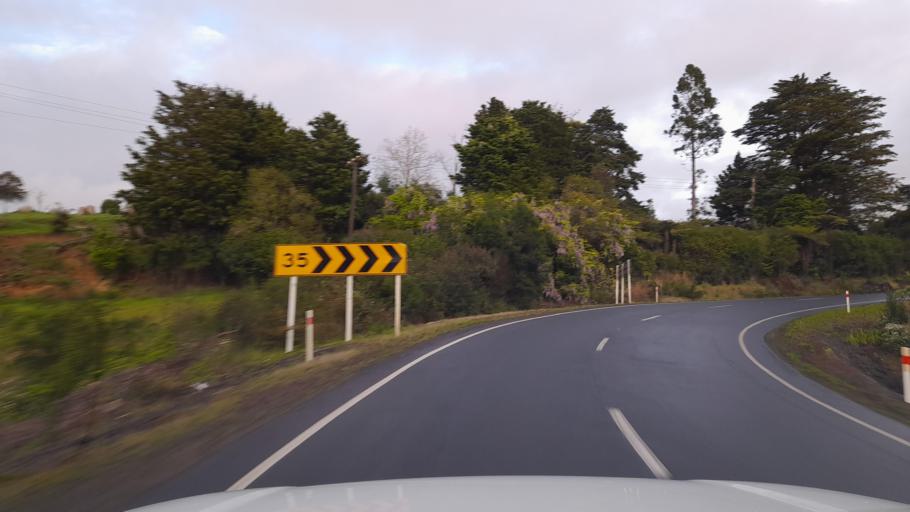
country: NZ
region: Northland
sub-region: Kaipara District
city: Dargaville
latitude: -35.7148
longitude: 173.9561
